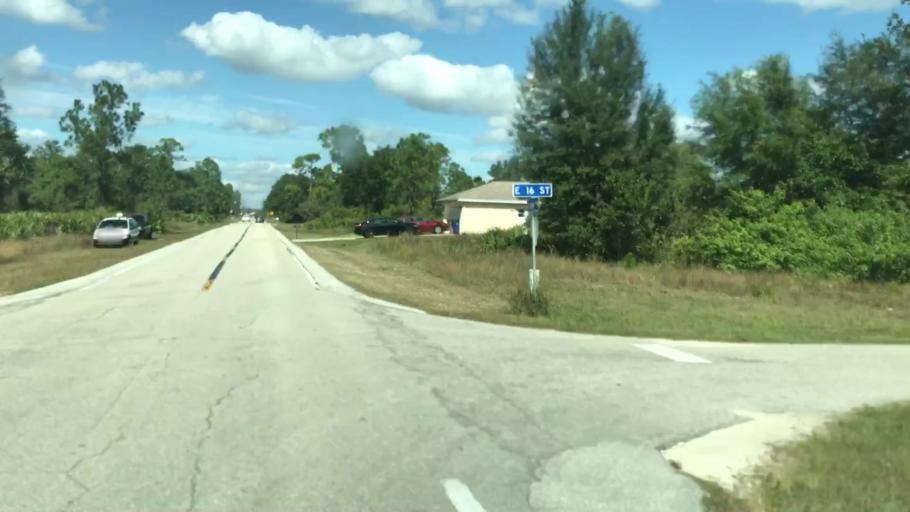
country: US
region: Florida
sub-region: Lee County
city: Lehigh Acres
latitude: 26.6582
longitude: -81.6255
